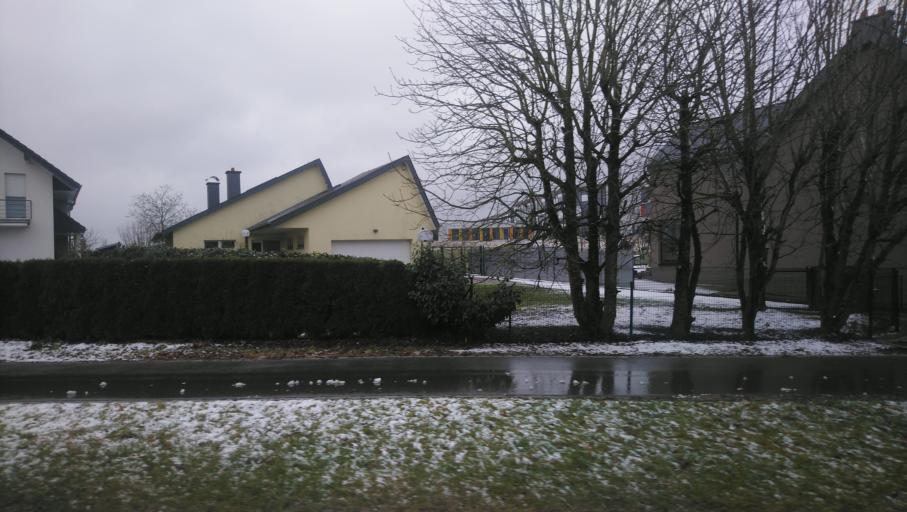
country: LU
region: Grevenmacher
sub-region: Canton de Grevenmacher
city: Junglinster
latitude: 49.7006
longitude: 6.2470
